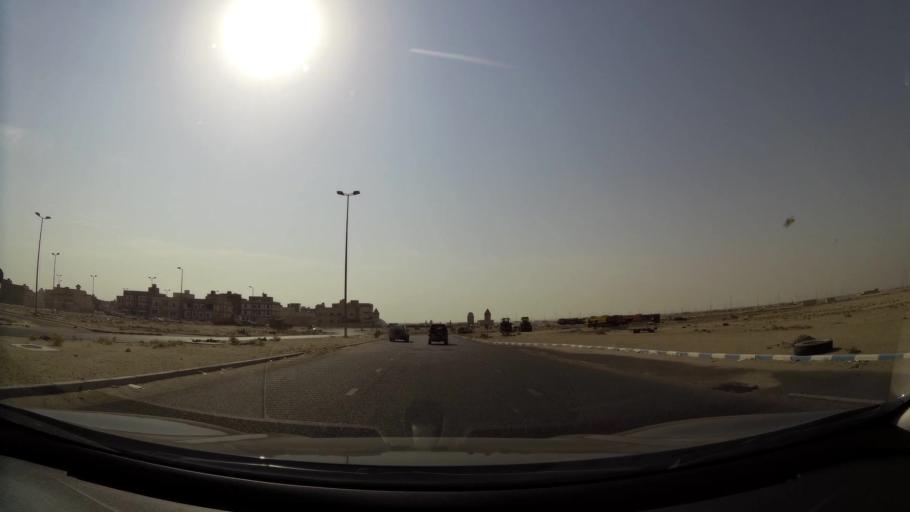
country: KW
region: Al Ahmadi
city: Al Wafrah
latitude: 28.7764
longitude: 48.0517
